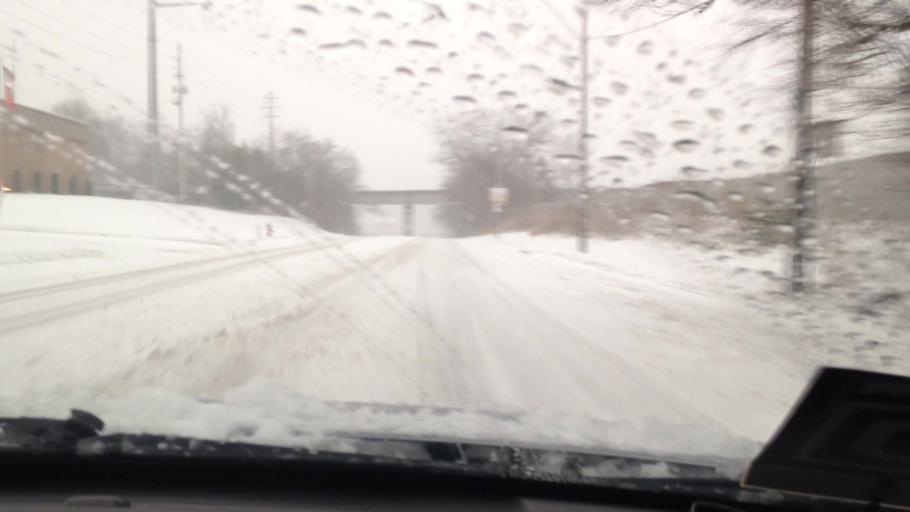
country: US
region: Missouri
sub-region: Jackson County
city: Raytown
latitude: 39.0598
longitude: -94.5017
